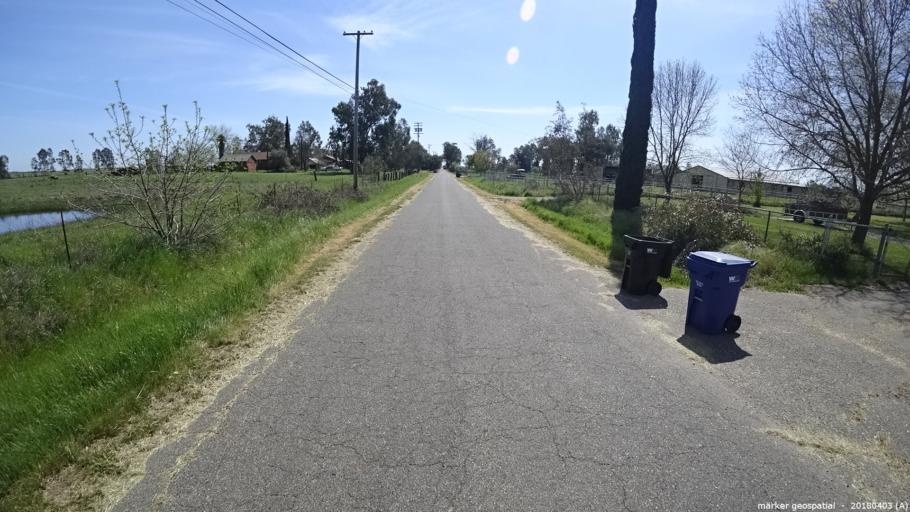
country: US
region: California
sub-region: Sacramento County
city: Clay
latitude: 38.3488
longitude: -121.2146
